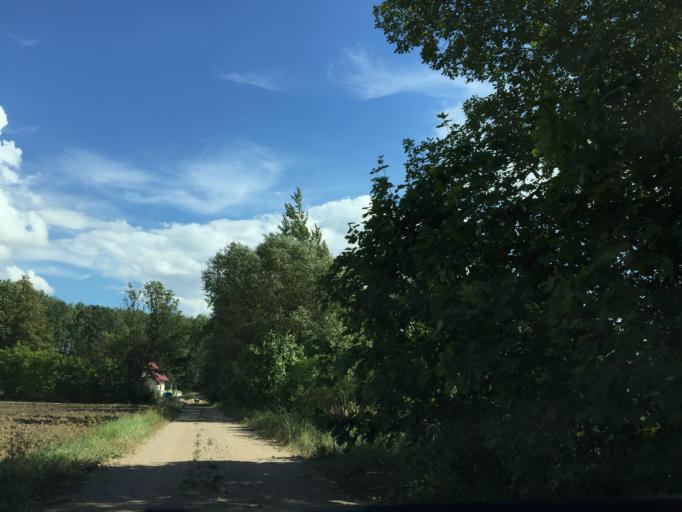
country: LT
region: Siauliu apskritis
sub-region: Joniskis
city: Joniskis
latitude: 56.3542
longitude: 23.5732
